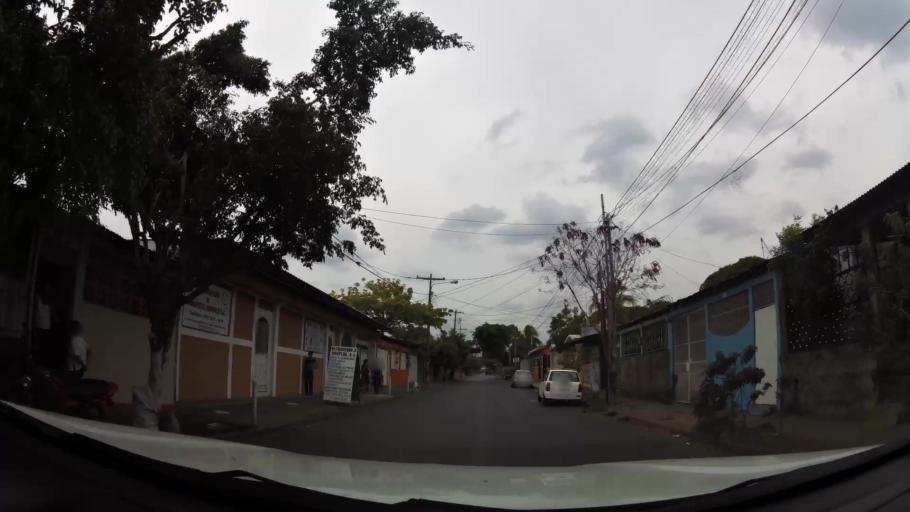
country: NI
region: Managua
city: Managua
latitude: 12.1278
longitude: -86.2275
